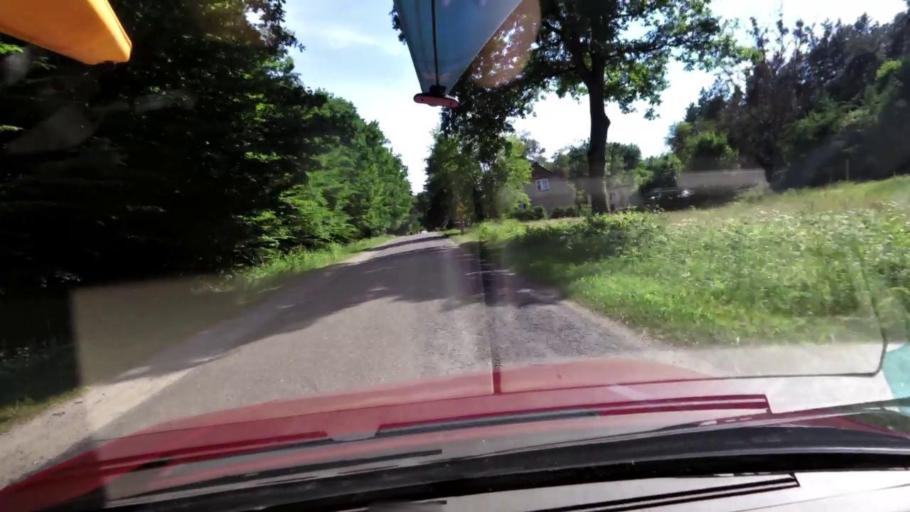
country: PL
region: Pomeranian Voivodeship
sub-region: Powiat slupski
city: Kepice
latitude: 54.1530
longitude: 16.9083
